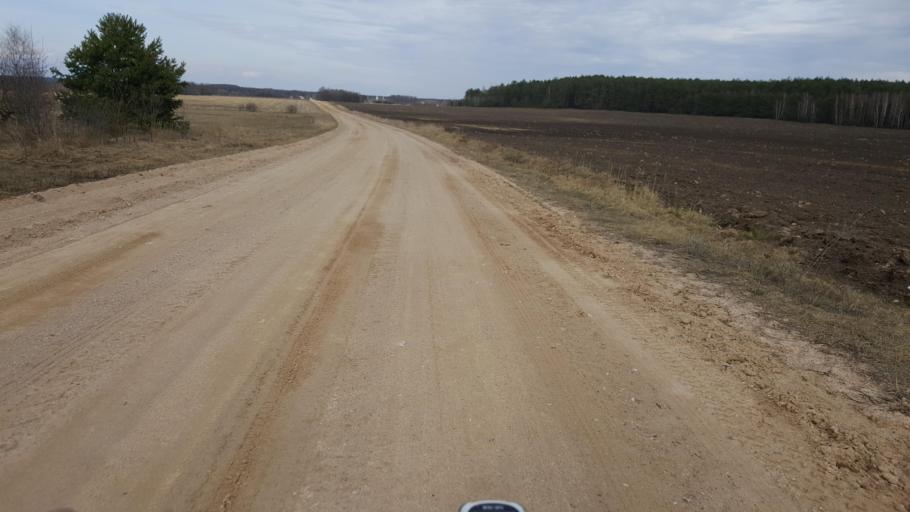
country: BY
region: Brest
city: Zhabinka
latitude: 52.3789
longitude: 23.9910
